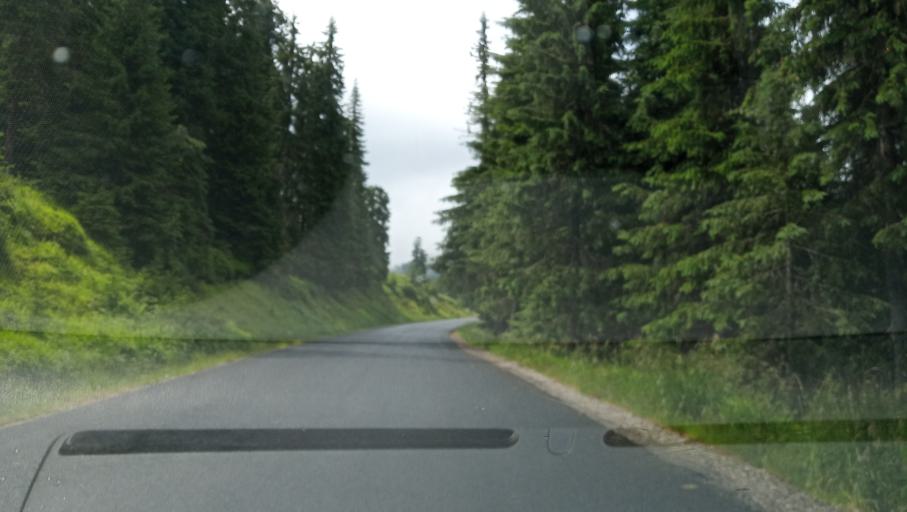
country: RO
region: Hunedoara
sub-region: Oras Petrila
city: Petrila
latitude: 45.4116
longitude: 23.5943
